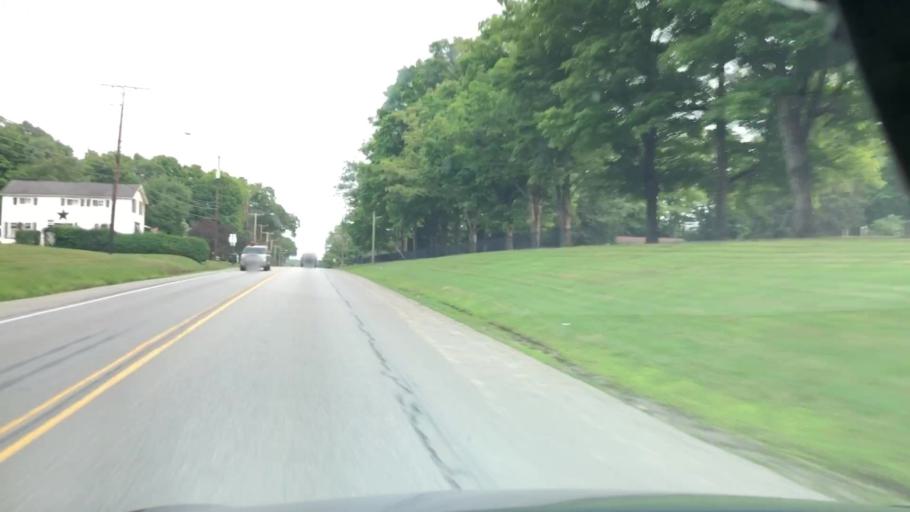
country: US
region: Pennsylvania
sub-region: Crawford County
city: Titusville
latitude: 41.6457
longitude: -79.7156
